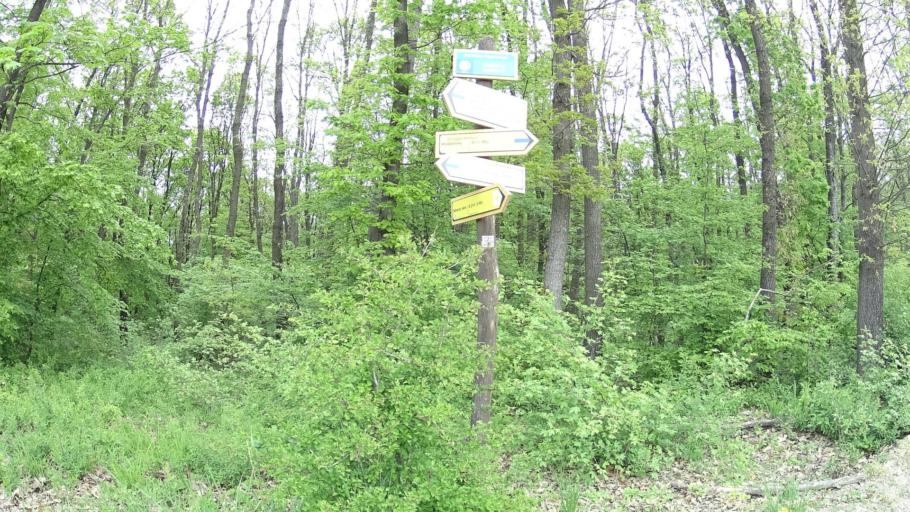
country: HU
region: Nograd
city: Romhany
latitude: 47.8950
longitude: 19.2458
